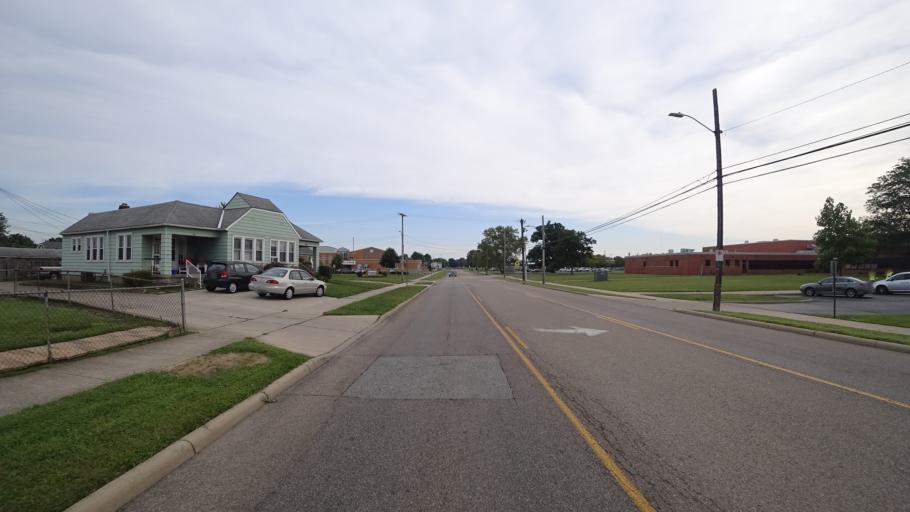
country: US
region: Ohio
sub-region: Butler County
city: Hamilton
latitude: 39.3951
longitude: -84.5423
